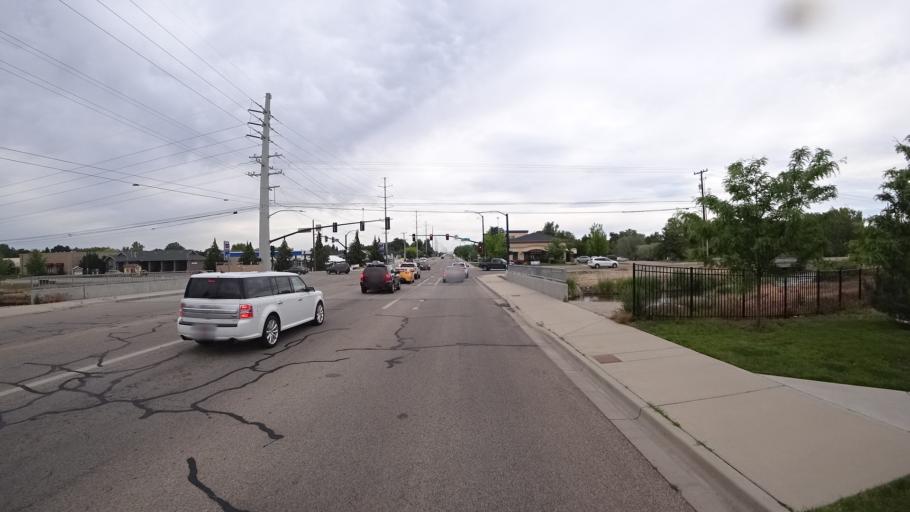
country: US
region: Idaho
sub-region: Ada County
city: Meridian
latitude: 43.5898
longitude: -116.3343
